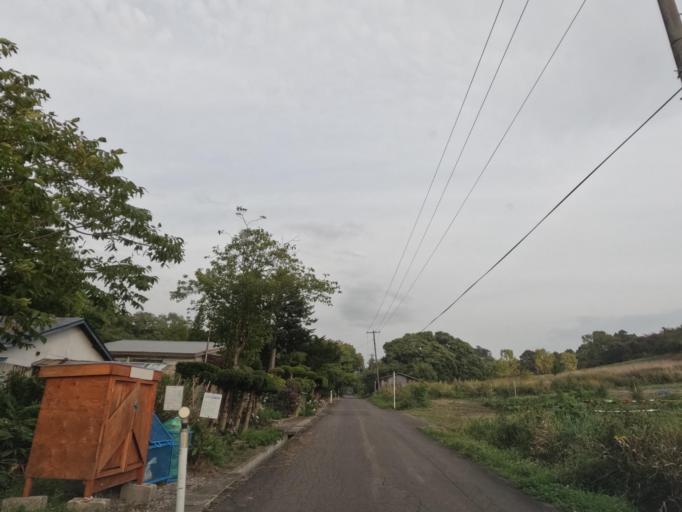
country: JP
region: Hokkaido
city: Date
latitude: 42.4128
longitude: 140.9200
